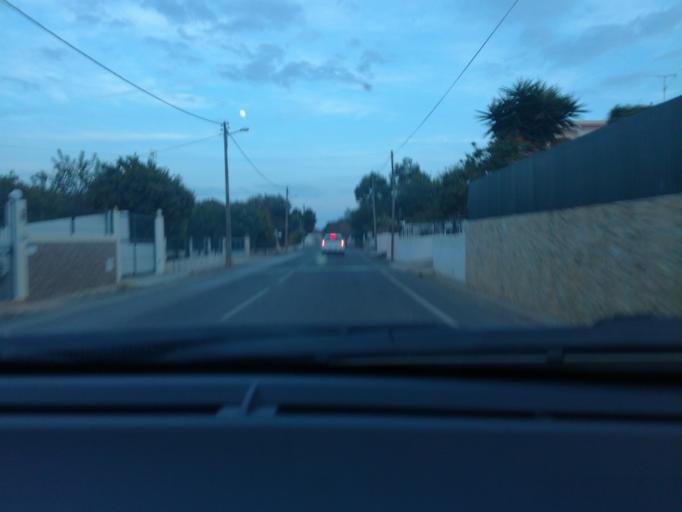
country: PT
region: Faro
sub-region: Olhao
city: Laranjeiro
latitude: 37.0617
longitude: -7.7553
